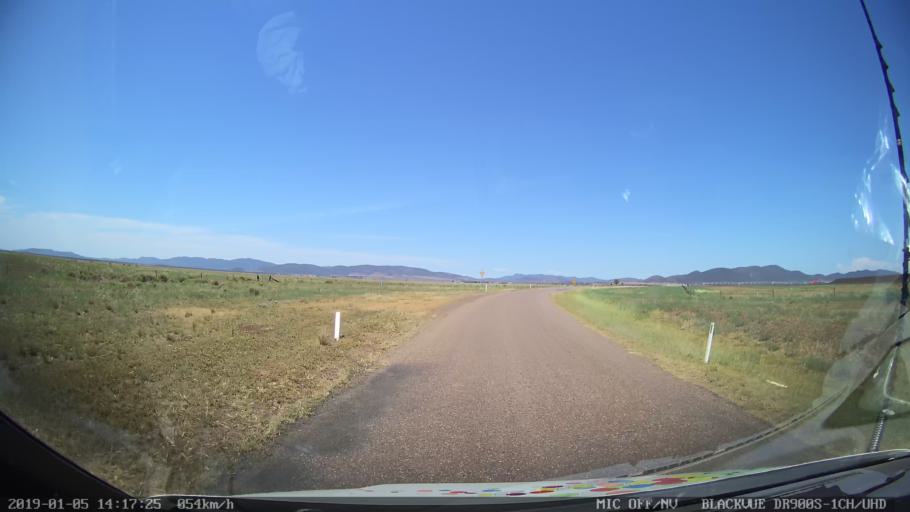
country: AU
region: New South Wales
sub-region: Liverpool Plains
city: Quirindi
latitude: -31.2545
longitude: 150.4772
